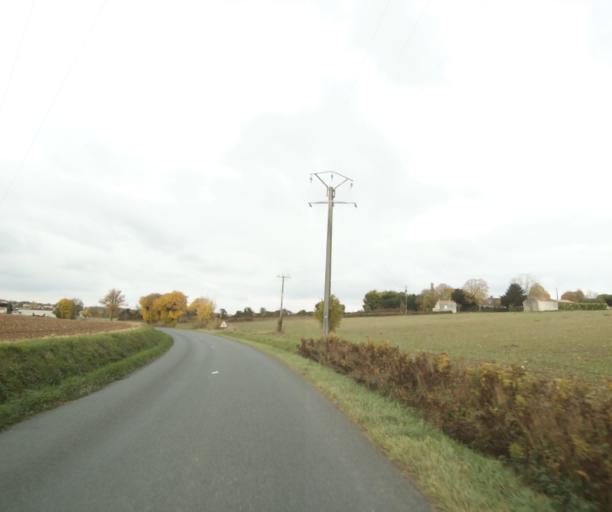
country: FR
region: Poitou-Charentes
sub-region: Departement de la Charente-Maritime
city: Bussac-sur-Charente
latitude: 45.7758
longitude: -0.6722
